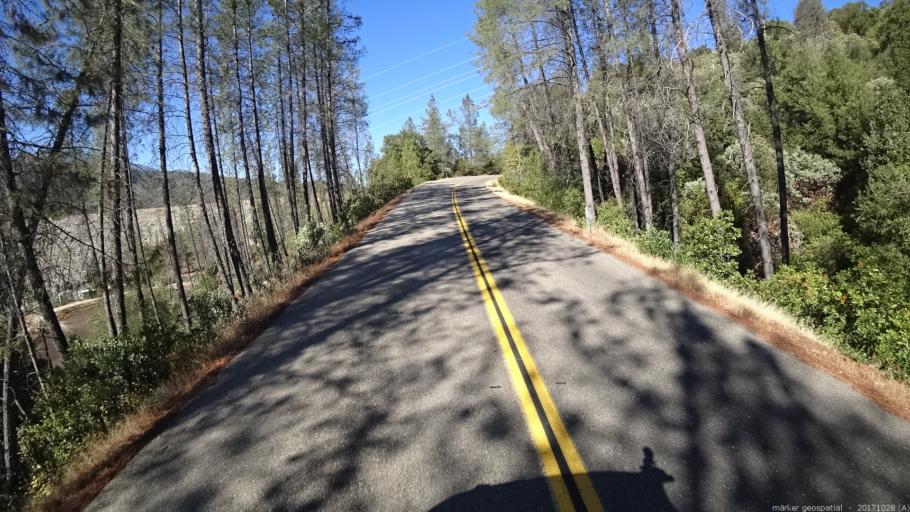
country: US
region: California
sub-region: Shasta County
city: Shasta
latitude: 40.5983
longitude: -122.5348
